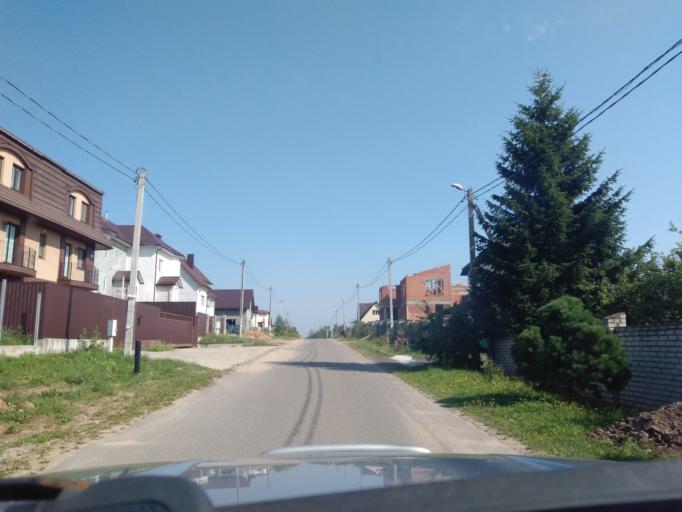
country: BY
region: Minsk
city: Zhdanovichy
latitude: 53.9358
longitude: 27.4026
